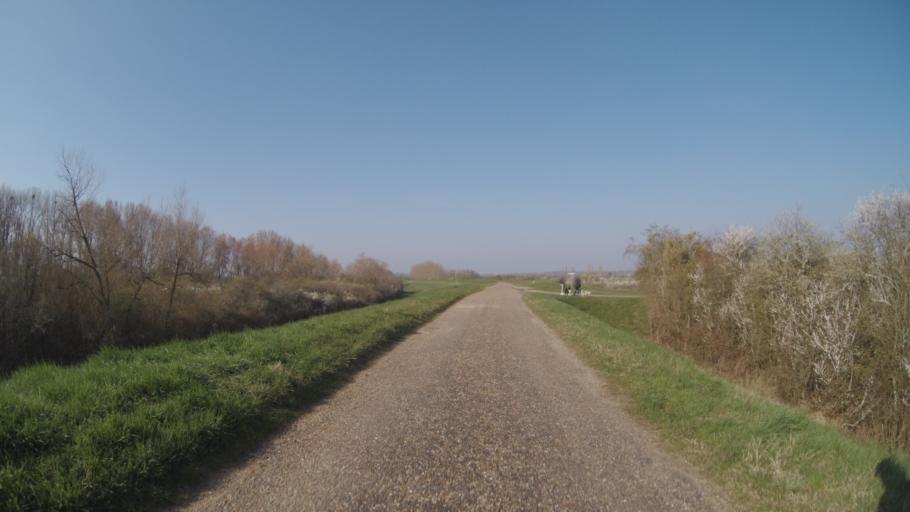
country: FR
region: Centre
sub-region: Departement du Loiret
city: Mardie
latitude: 47.8713
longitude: 2.0366
